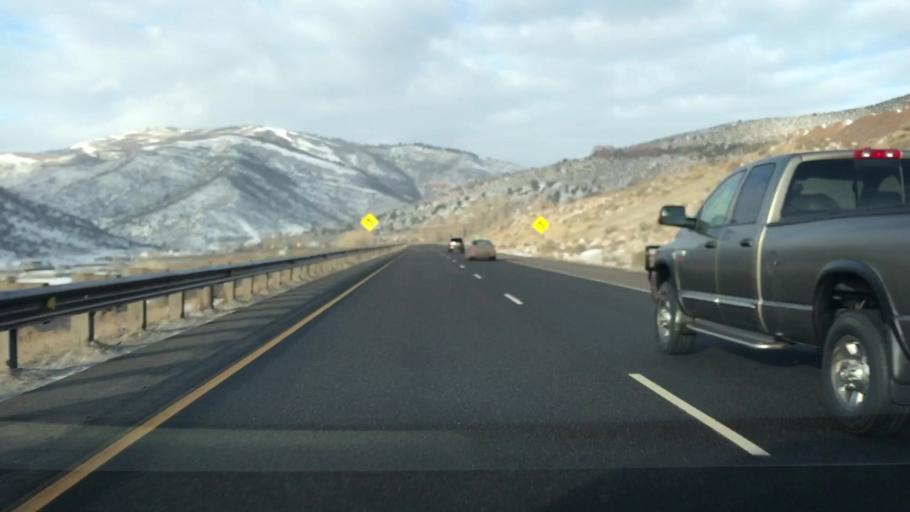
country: US
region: Colorado
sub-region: Eagle County
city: Edwards
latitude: 39.6558
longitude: -106.6174
